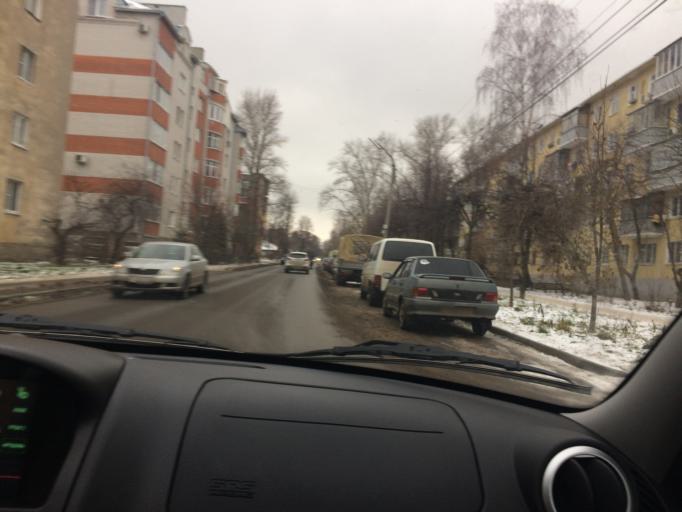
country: RU
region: Rjazan
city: Ryazan'
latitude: 54.6188
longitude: 39.7179
